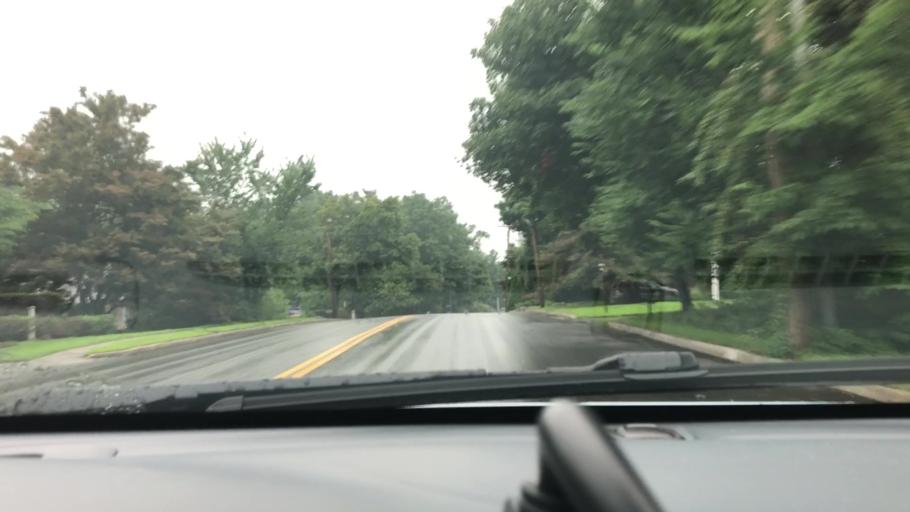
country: US
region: New Hampshire
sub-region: Hillsborough County
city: Manchester
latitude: 43.0170
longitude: -71.4620
